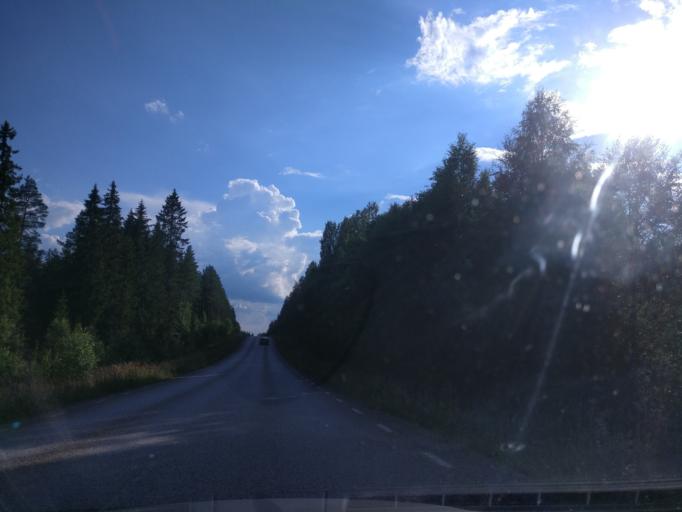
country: SE
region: Dalarna
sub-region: Ludvika Kommun
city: Ludvika
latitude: 60.2823
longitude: 15.0918
